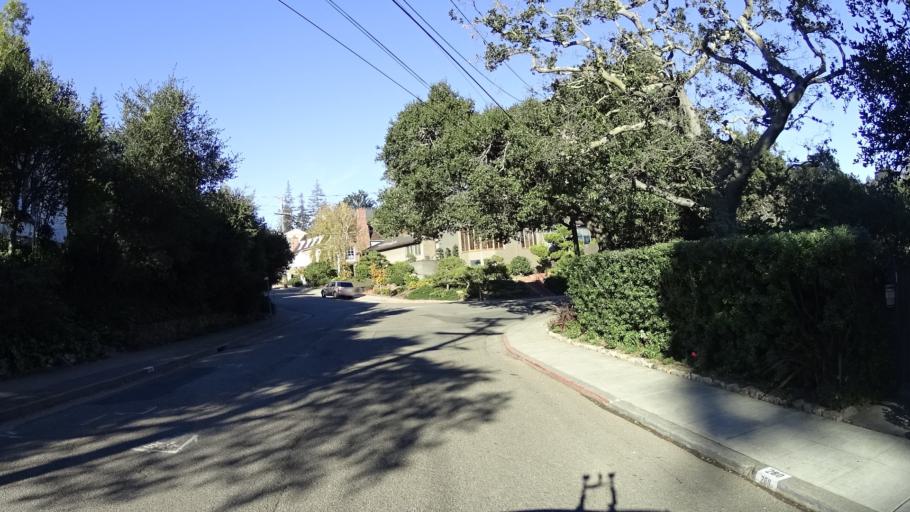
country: US
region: California
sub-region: Alameda County
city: Piedmont
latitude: 37.8153
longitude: -122.2217
